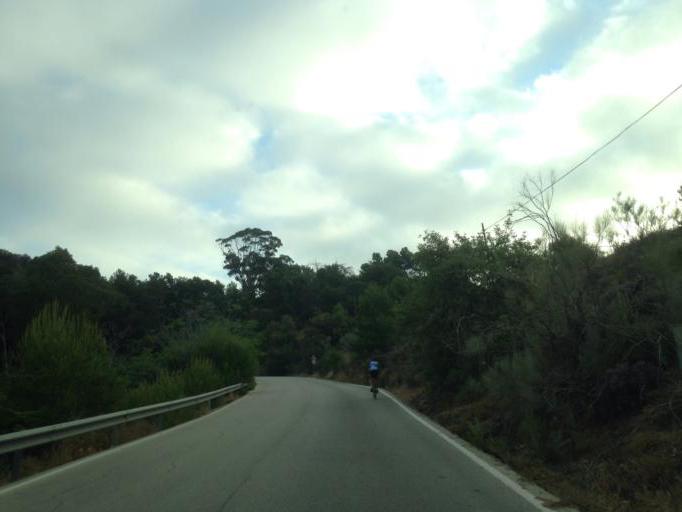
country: ES
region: Andalusia
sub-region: Provincia de Malaga
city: Malaga
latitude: 36.7591
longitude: -4.4078
